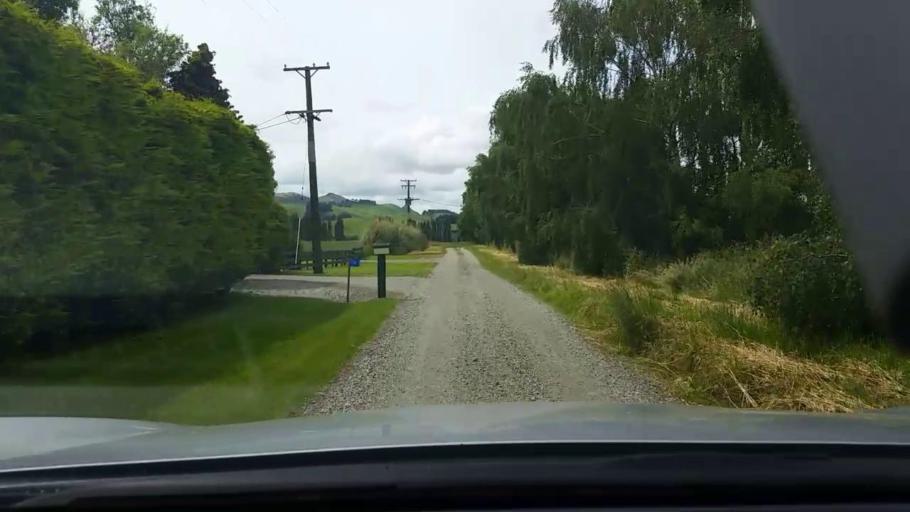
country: NZ
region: Southland
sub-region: Gore District
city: Gore
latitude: -46.1237
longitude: 168.9302
